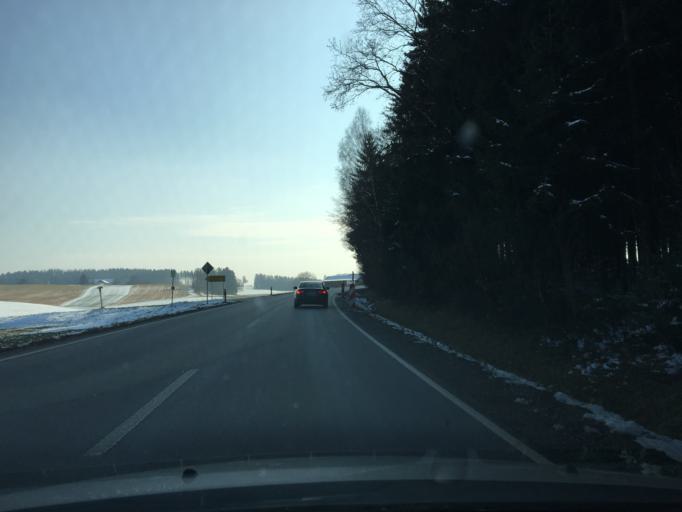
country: DE
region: Bavaria
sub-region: Lower Bavaria
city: Marklkofen
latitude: 48.4972
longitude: 12.5690
